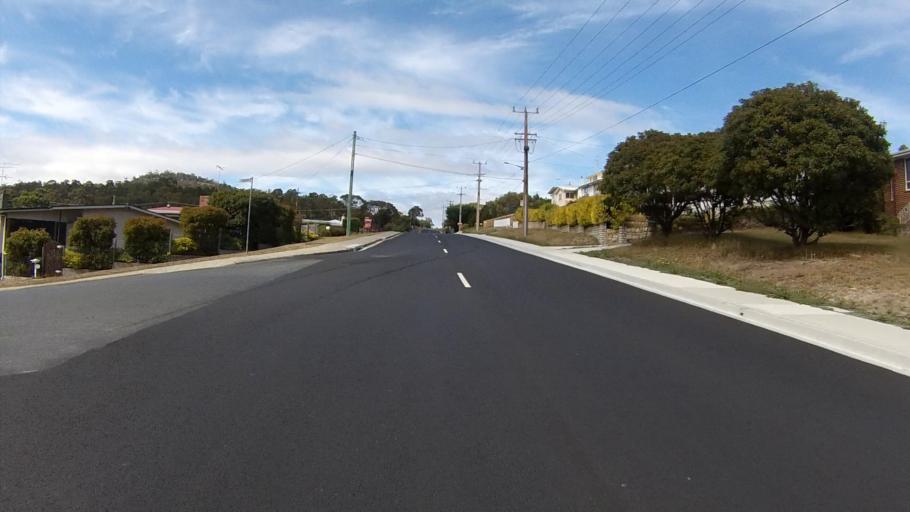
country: AU
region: Tasmania
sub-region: Clarence
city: Lindisfarne
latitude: -42.8134
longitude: 147.3513
